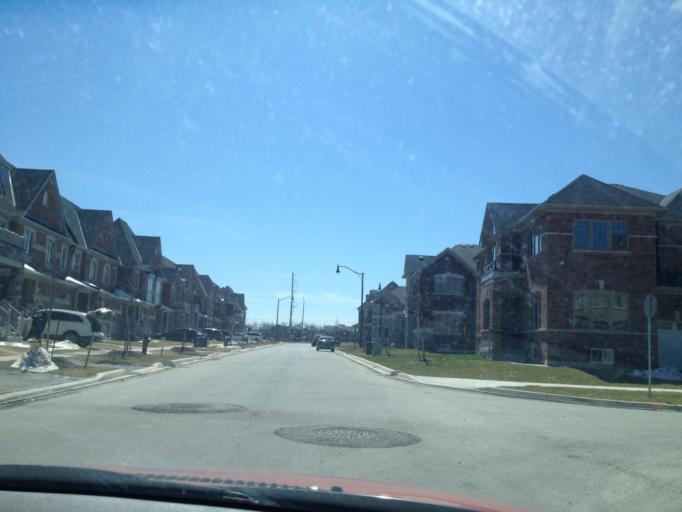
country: CA
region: Ontario
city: Brampton
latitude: 43.7035
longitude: -79.8522
